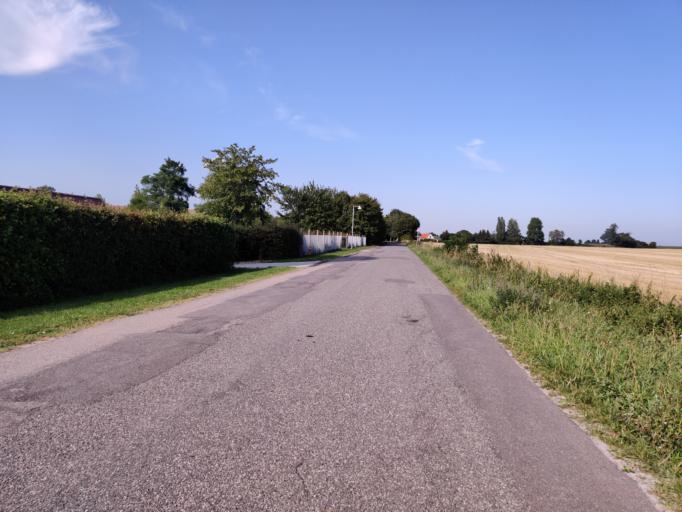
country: DK
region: Zealand
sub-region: Guldborgsund Kommune
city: Nykobing Falster
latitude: 54.7174
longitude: 11.9276
